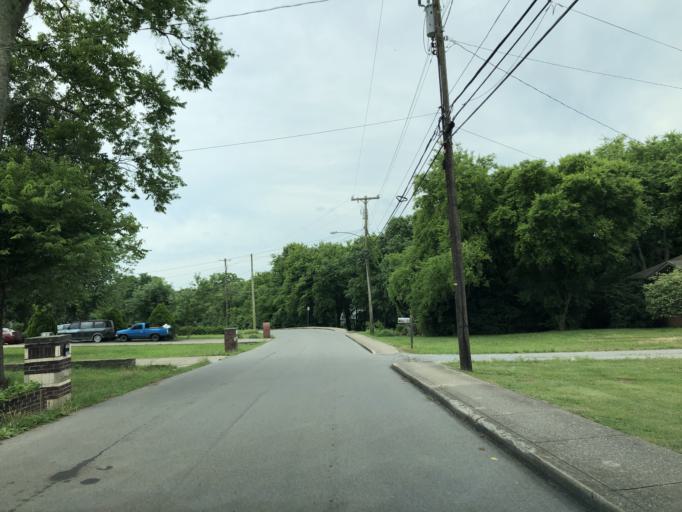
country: US
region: Tennessee
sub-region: Davidson County
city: Goodlettsville
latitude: 36.2902
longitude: -86.7106
